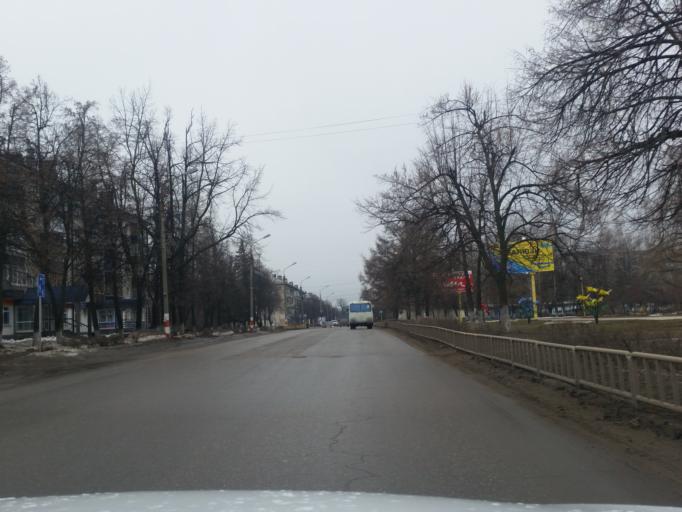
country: RU
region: Ulyanovsk
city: Dimitrovgrad
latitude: 54.2290
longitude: 49.5510
